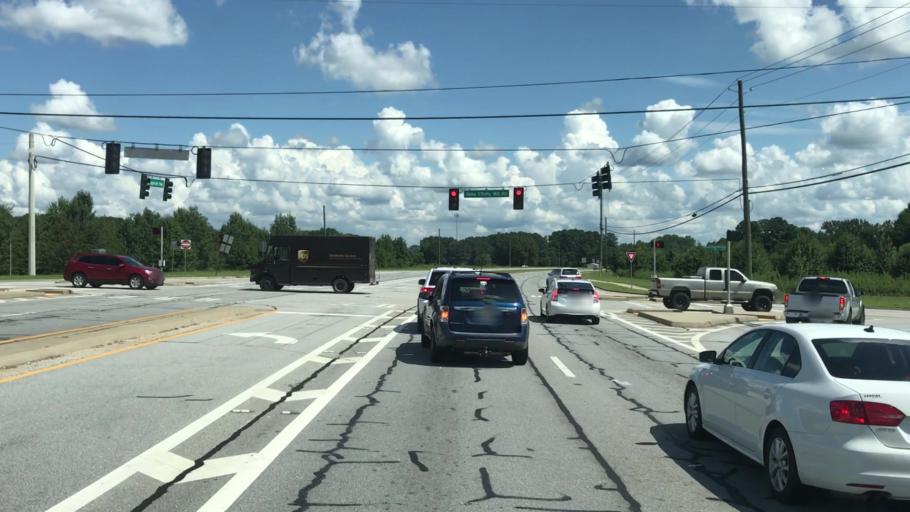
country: US
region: Georgia
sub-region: Walton County
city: Loganville
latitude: 33.8675
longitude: -83.9113
